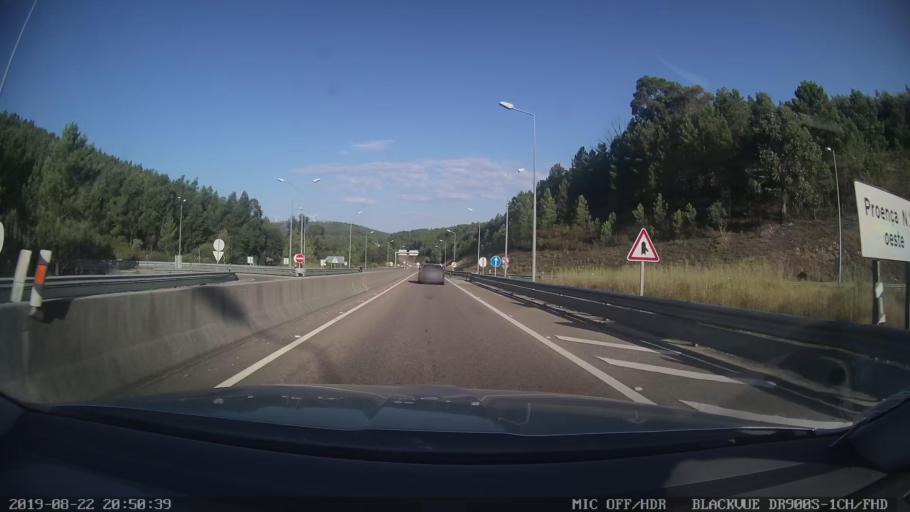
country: PT
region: Castelo Branco
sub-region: Proenca-A-Nova
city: Proenca-a-Nova
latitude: 39.7563
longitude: -7.9427
